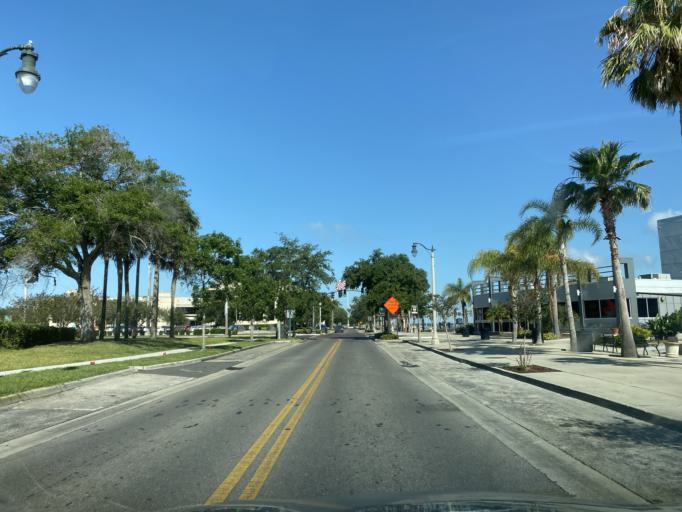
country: US
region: Florida
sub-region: Seminole County
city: Sanford
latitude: 28.8138
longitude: -81.2653
